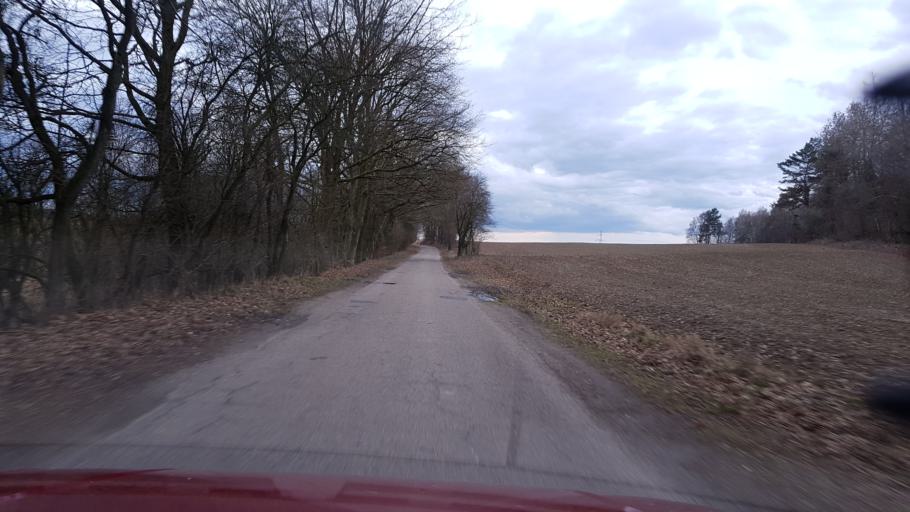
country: PL
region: West Pomeranian Voivodeship
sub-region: Powiat gryfinski
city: Stare Czarnowo
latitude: 53.3341
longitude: 14.6659
